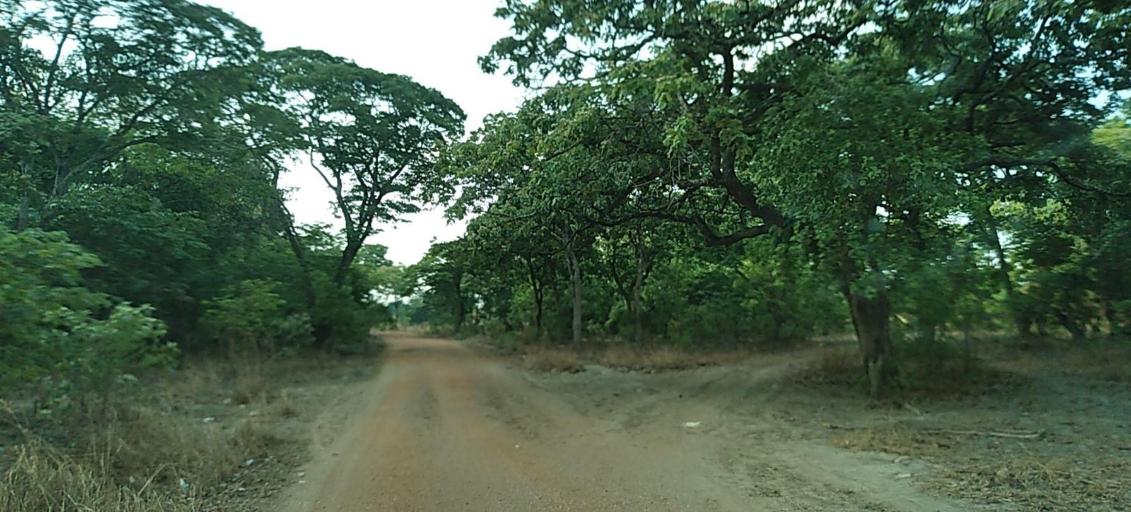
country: ZM
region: Copperbelt
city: Mpongwe
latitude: -13.4778
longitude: 28.0829
